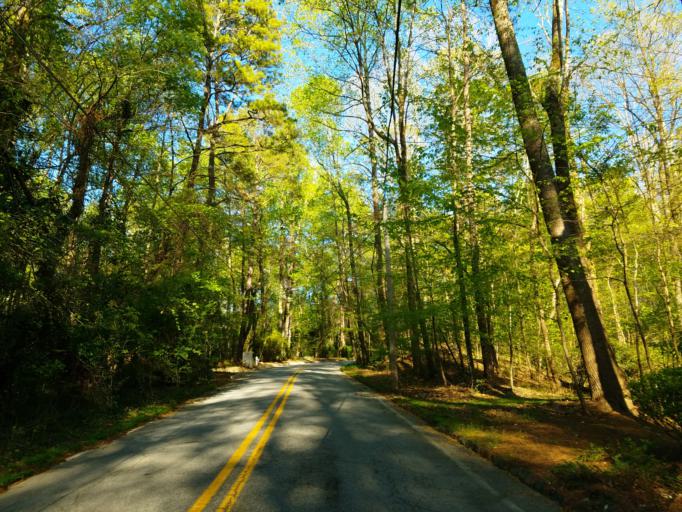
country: US
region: Georgia
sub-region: Cobb County
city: Vinings
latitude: 33.8431
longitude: -84.4553
